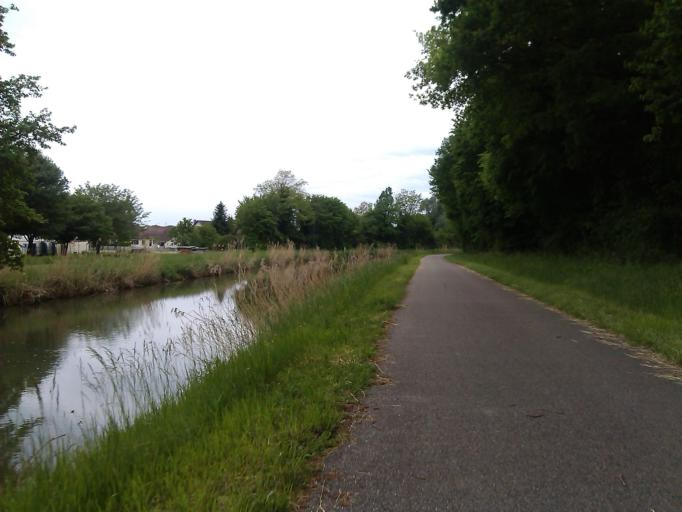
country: FR
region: Franche-Comte
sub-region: Departement du Jura
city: Damparis
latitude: 47.0727
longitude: 5.3659
